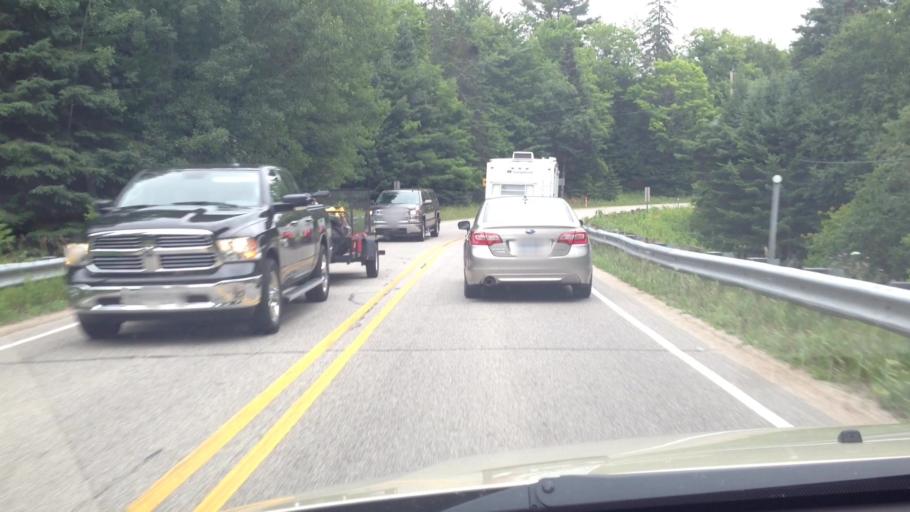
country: US
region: Michigan
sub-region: Mackinac County
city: Saint Ignace
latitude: 46.0524
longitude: -85.1101
